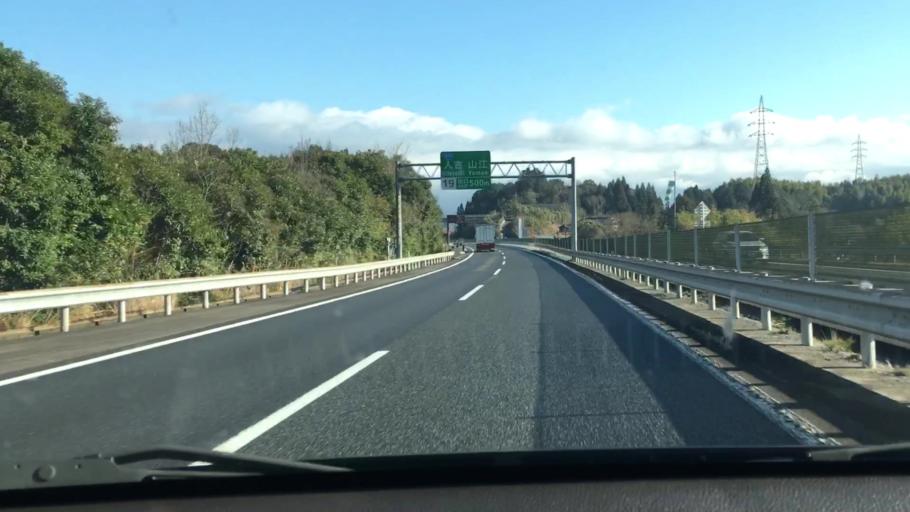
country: JP
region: Kumamoto
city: Hitoyoshi
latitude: 32.2358
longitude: 130.7640
